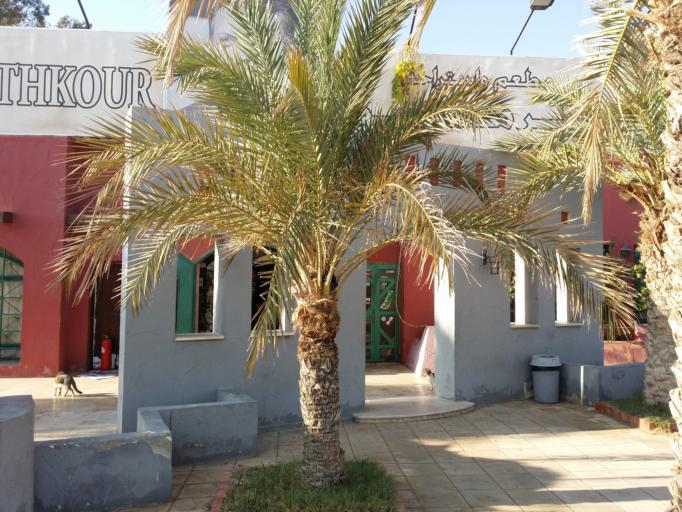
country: JO
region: Ma'an
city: Petra
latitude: 30.4698
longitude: 35.2906
